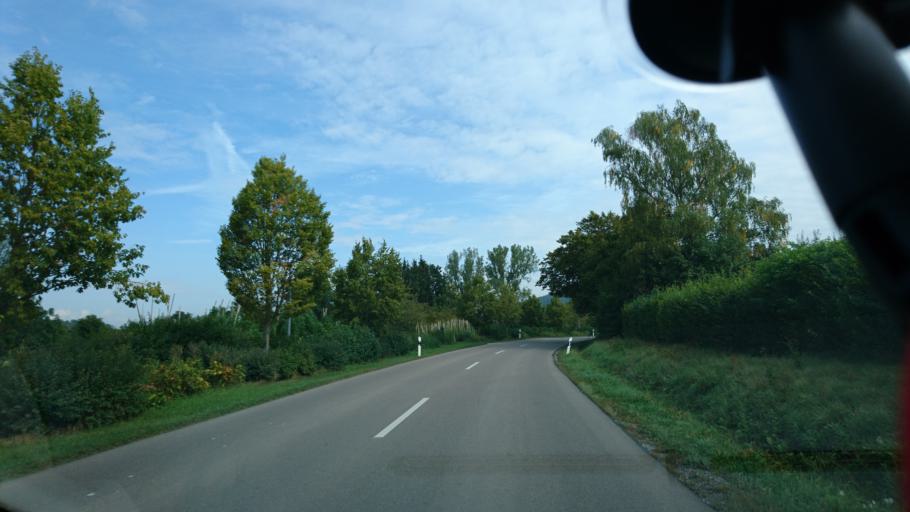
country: DE
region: Baden-Wuerttemberg
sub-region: Regierungsbezirk Stuttgart
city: Vellberg
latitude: 49.0930
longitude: 9.8842
